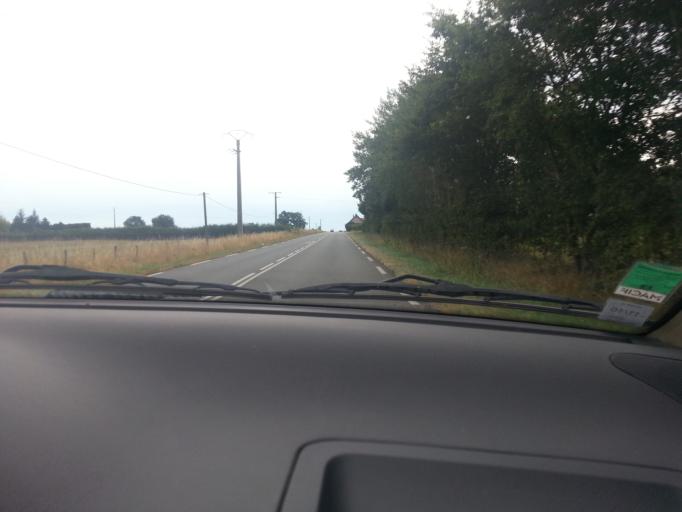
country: FR
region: Auvergne
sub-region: Departement de l'Allier
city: Saint-Gerand-le-Puy
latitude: 46.2098
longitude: 3.5162
